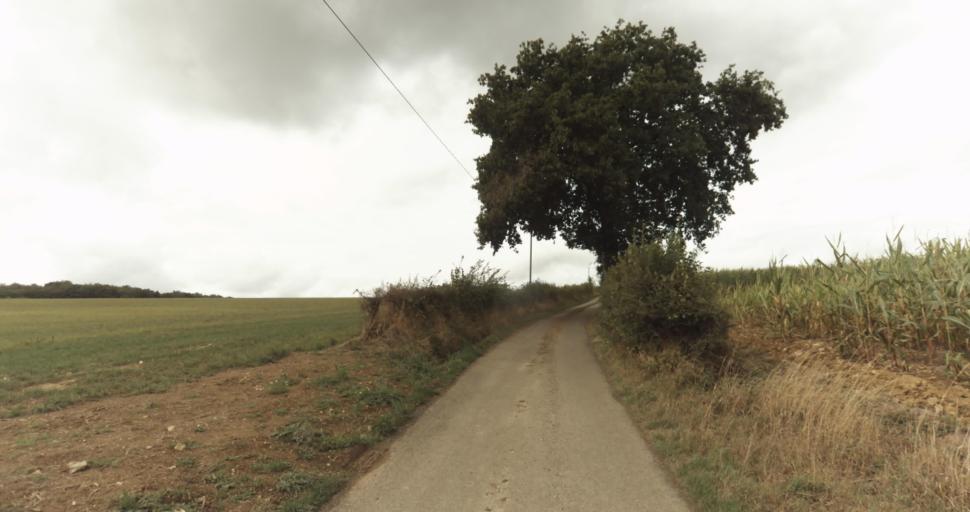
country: FR
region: Lower Normandy
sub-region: Departement de l'Orne
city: Gace
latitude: 48.8237
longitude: 0.3649
